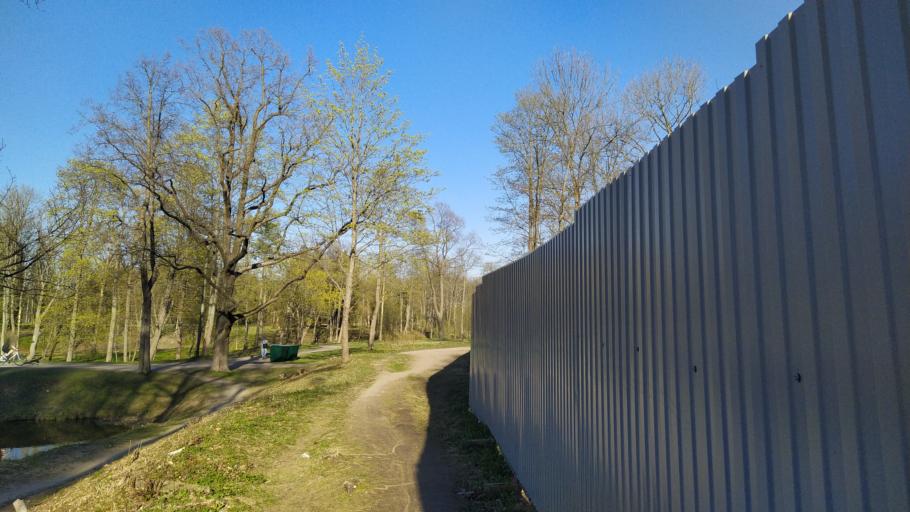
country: RU
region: St.-Petersburg
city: Aleksandrovskaya
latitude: 59.7089
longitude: 30.3445
